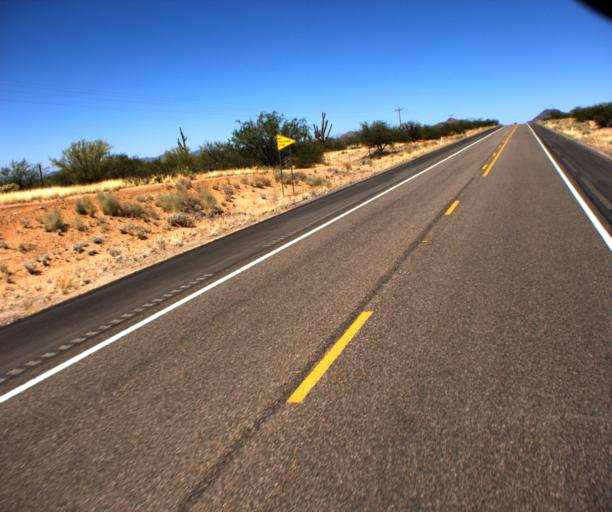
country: US
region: Arizona
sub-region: Pima County
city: Three Points
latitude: 32.0299
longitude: -111.5633
